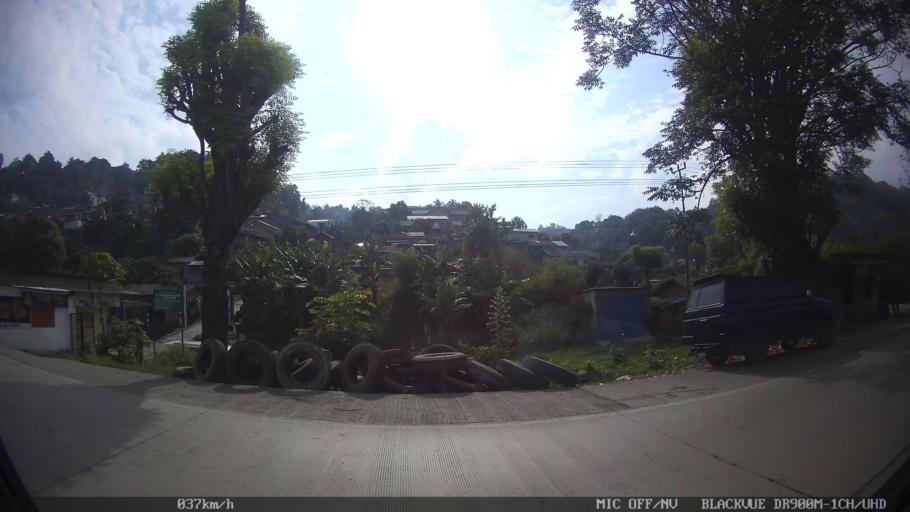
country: ID
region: Lampung
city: Panjang
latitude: -5.4778
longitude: 105.3256
